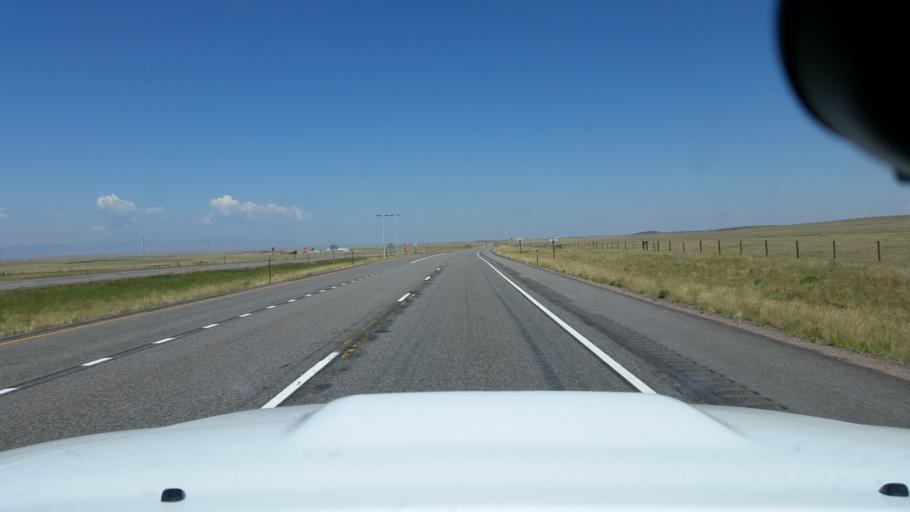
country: US
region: Wyoming
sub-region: Albany County
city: Laramie
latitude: 41.0920
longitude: -105.5188
